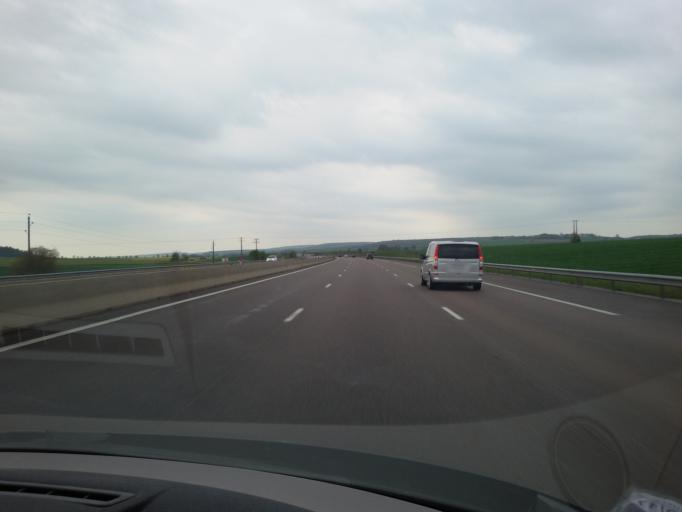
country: FR
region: Champagne-Ardenne
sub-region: Departement de la Haute-Marne
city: Rolampont
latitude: 47.8893
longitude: 5.2236
